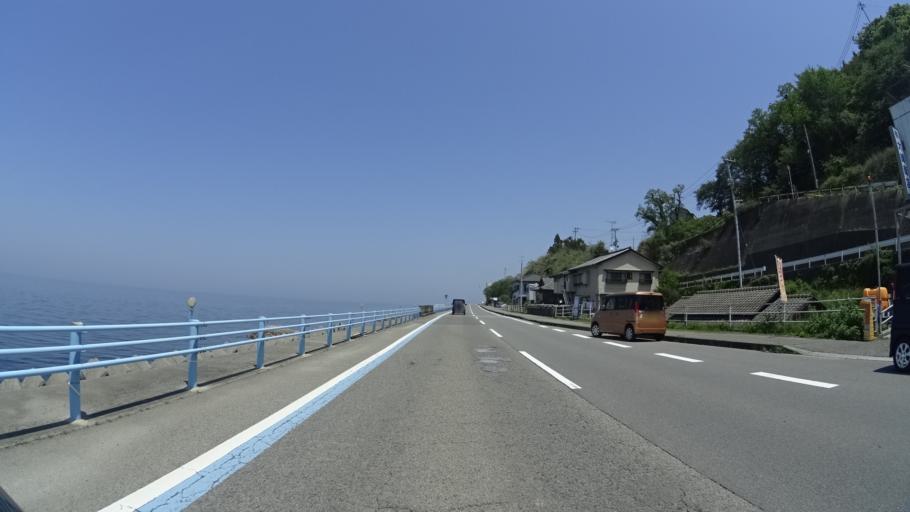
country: JP
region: Ehime
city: Iyo
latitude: 33.6703
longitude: 132.6105
